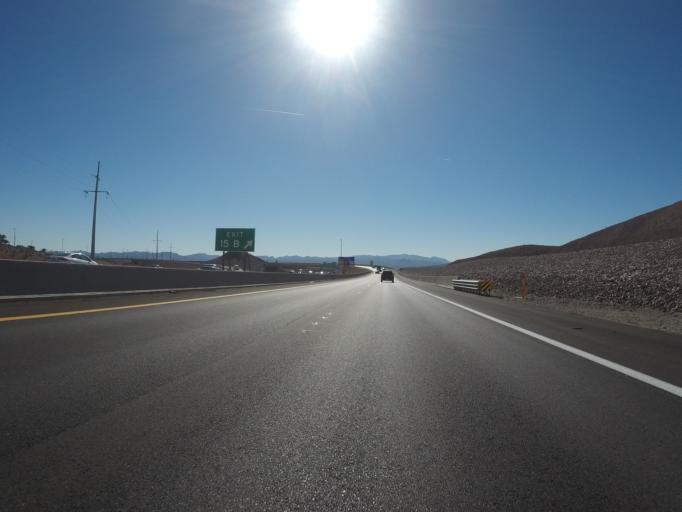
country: US
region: Nevada
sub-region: Clark County
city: Boulder City
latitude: 35.9729
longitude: -114.9145
